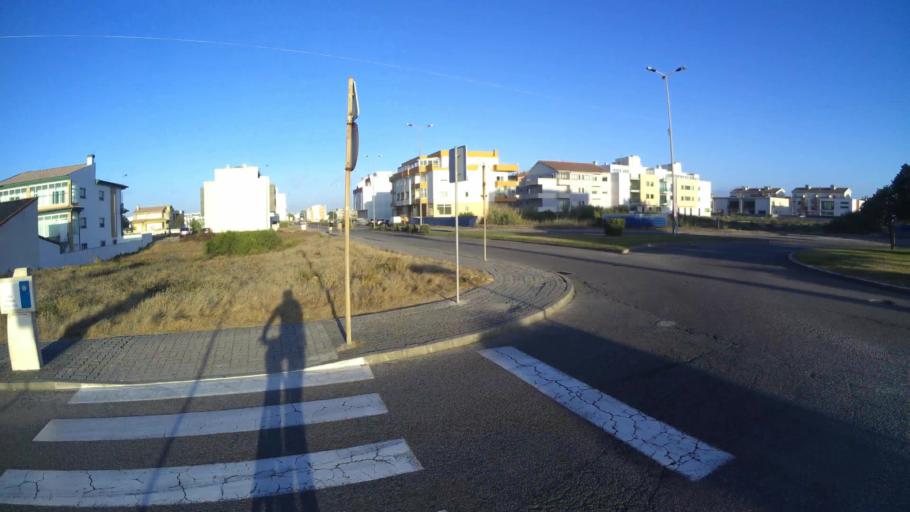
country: PT
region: Aveiro
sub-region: Ilhavo
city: Gafanha da Encarnacao
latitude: 40.5628
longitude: -8.7676
